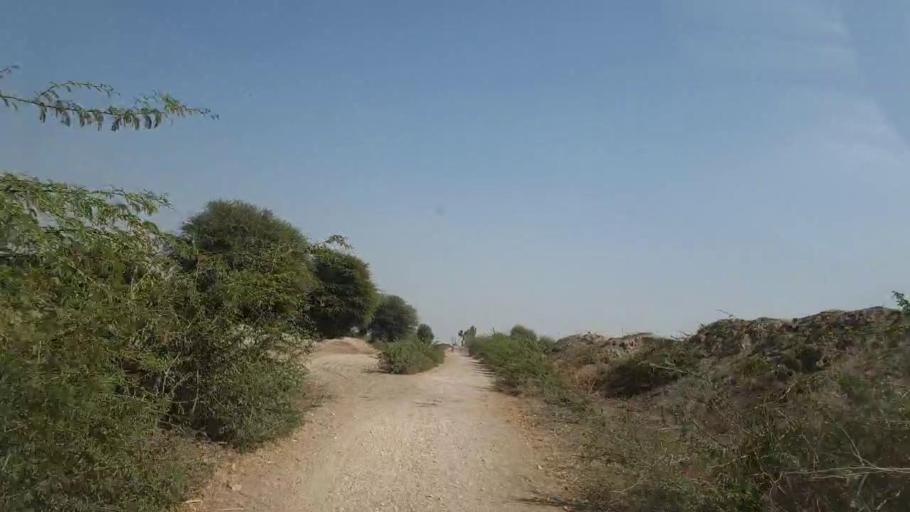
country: PK
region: Sindh
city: Nabisar
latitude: 25.0751
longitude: 69.5429
